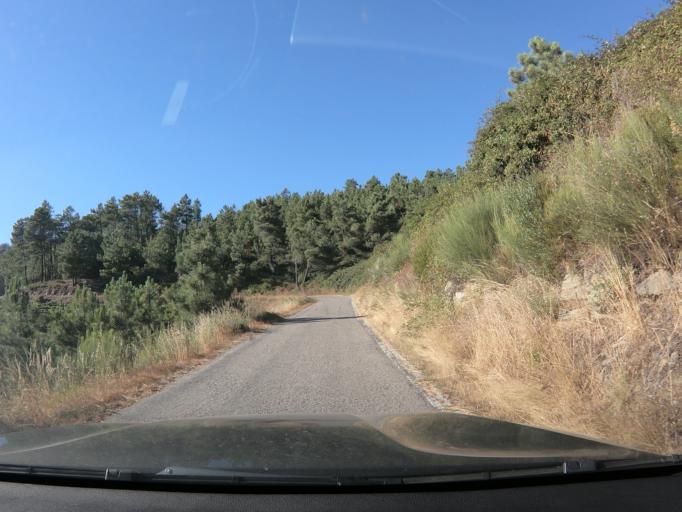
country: PT
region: Vila Real
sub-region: Sabrosa
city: Vilela
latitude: 41.2237
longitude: -7.5900
